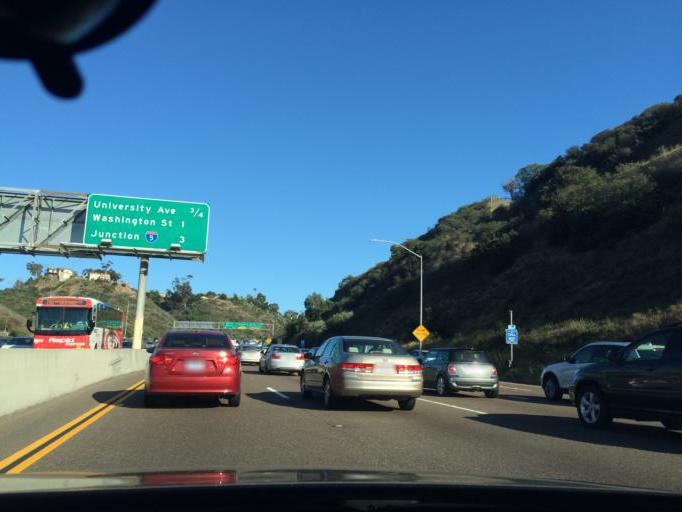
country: US
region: California
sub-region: San Diego County
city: San Diego
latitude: 32.7590
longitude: -117.1616
